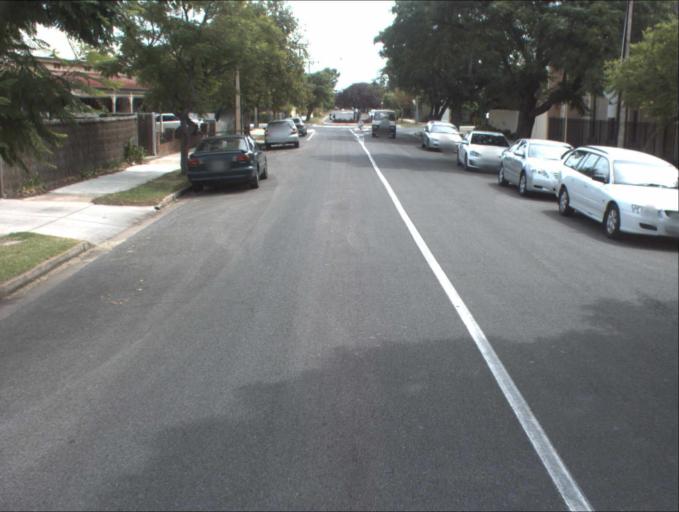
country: AU
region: South Australia
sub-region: Port Adelaide Enfield
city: Alberton
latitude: -34.8590
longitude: 138.5187
